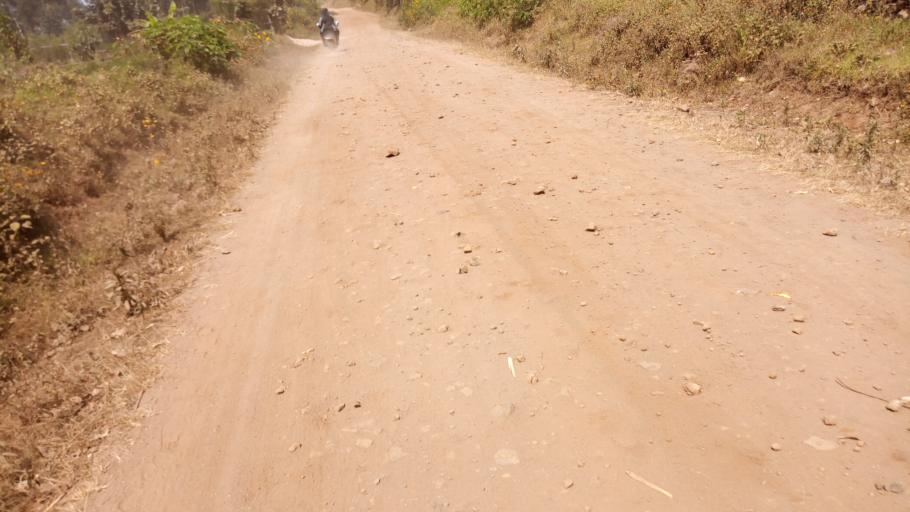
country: UG
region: Western Region
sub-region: Kisoro District
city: Kisoro
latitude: -1.3142
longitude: 29.7152
